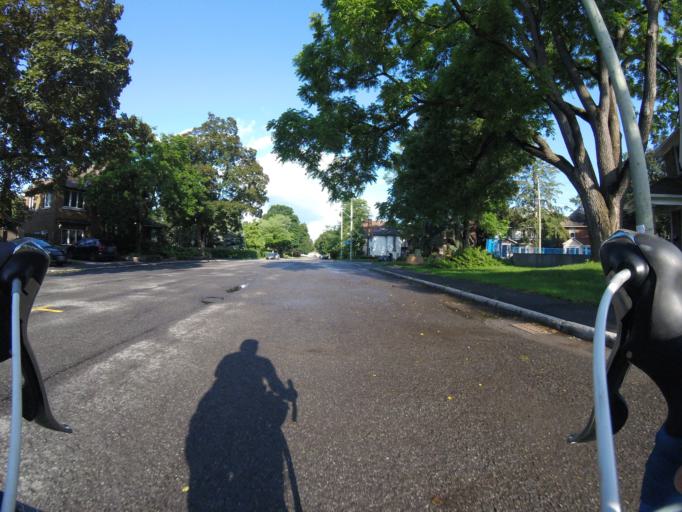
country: CA
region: Ontario
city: Ottawa
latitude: 45.4035
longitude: -75.6777
